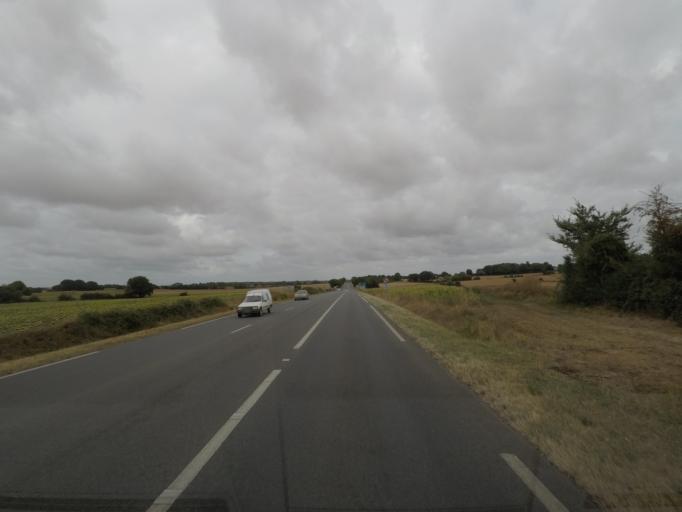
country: FR
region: Poitou-Charentes
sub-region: Departement des Deux-Sevres
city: Thorigne
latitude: 46.2777
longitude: -0.2475
